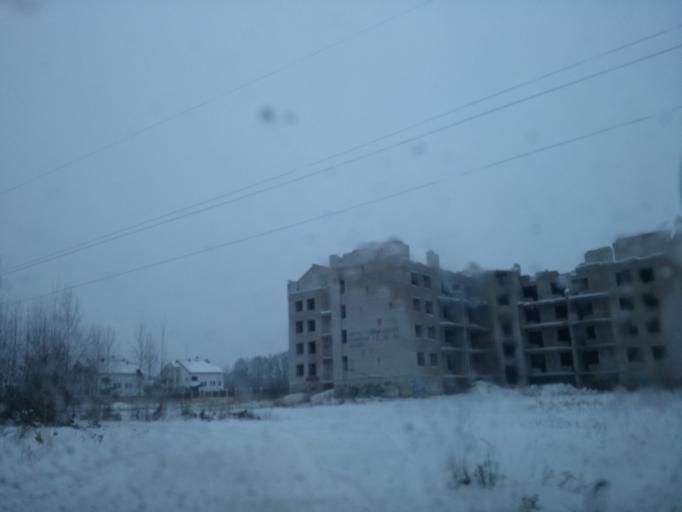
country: RU
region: Tverskaya
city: Tver
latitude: 56.8676
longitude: 35.8344
